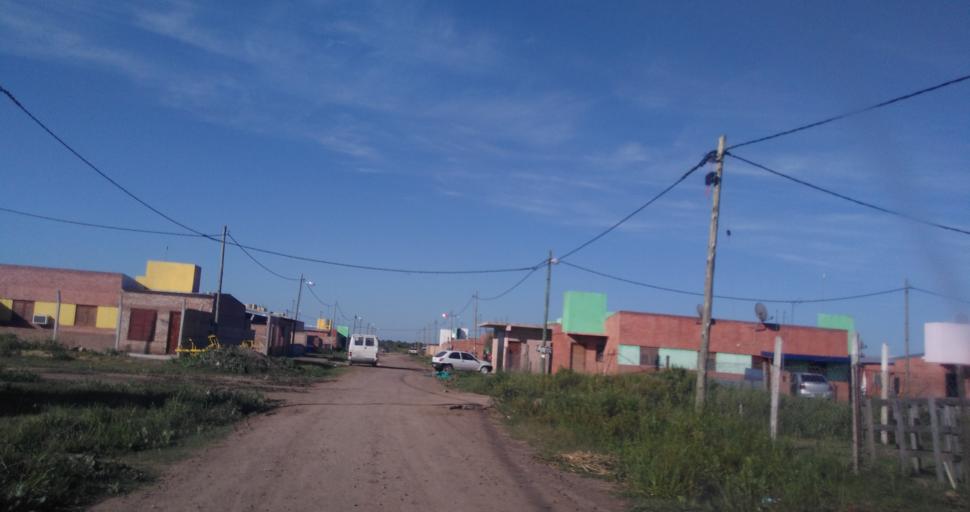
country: AR
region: Chaco
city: Resistencia
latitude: -27.4713
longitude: -59.0241
